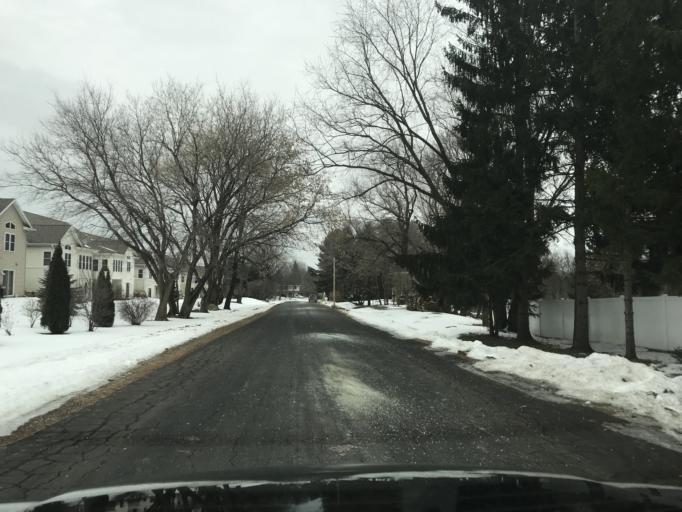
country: US
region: Wisconsin
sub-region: Dane County
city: Monona
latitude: 43.0832
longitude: -89.2707
